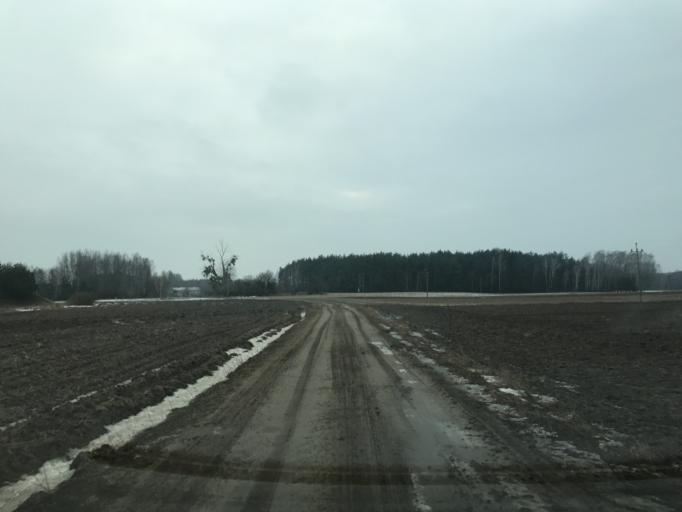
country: PL
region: Kujawsko-Pomorskie
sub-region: Powiat brodnicki
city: Brzozie
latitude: 53.2978
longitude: 19.5662
